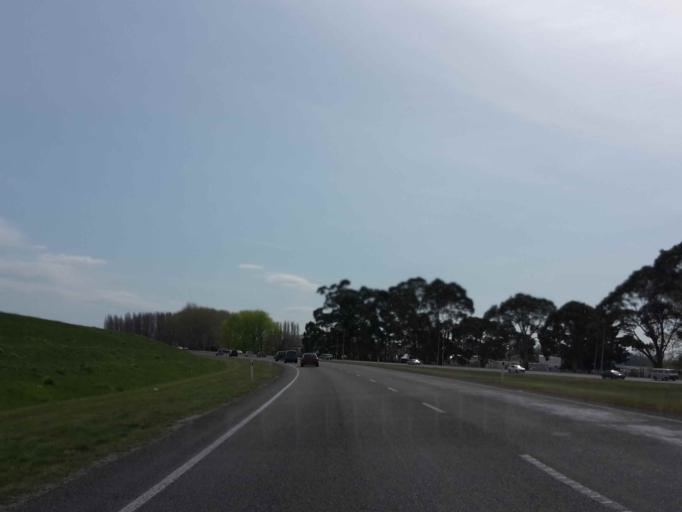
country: NZ
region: Canterbury
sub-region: Waimakariri District
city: Kaiapoi
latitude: -43.4243
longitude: 172.6483
